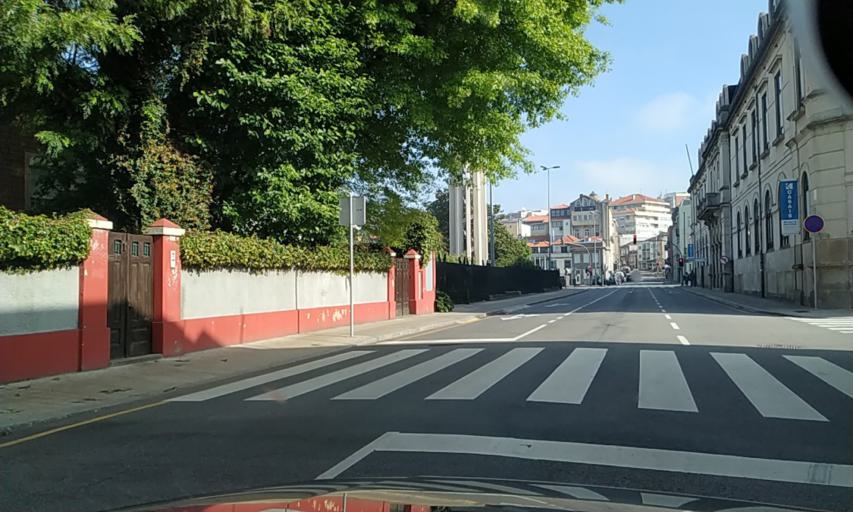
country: PT
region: Porto
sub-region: Porto
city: Porto
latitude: 41.1547
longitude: -8.6209
